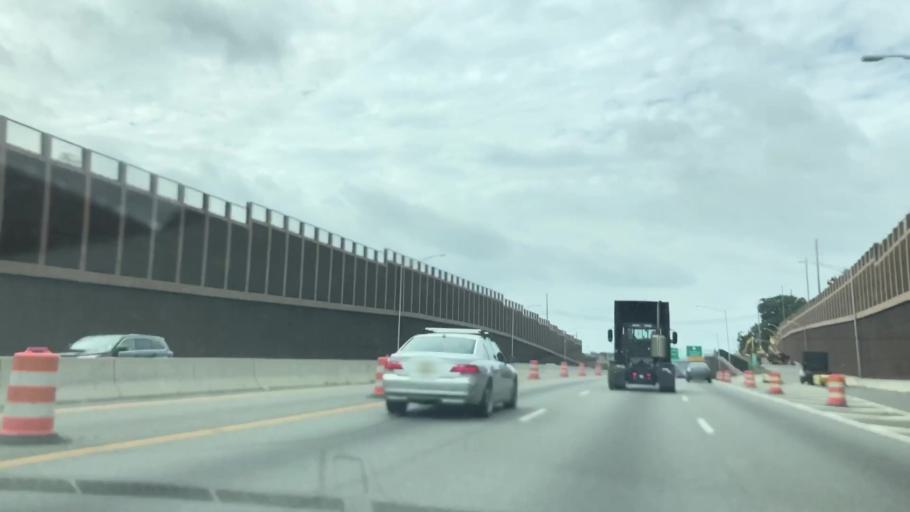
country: US
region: New Jersey
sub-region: Bergen County
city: Rutherford
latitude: 40.8151
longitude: -74.1103
